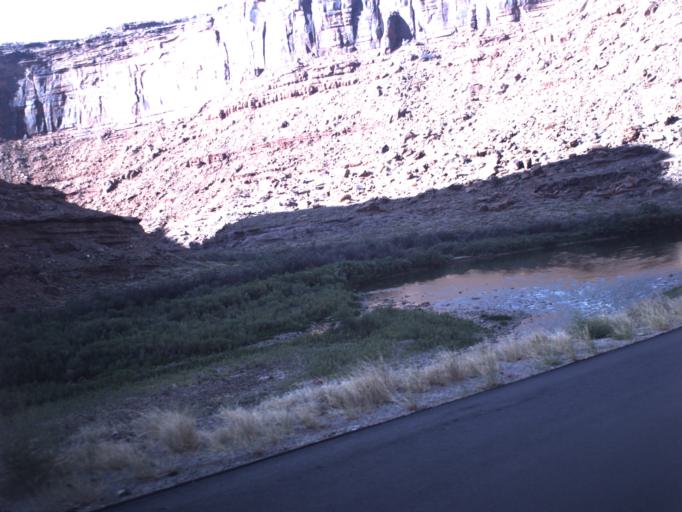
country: US
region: Utah
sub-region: Grand County
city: Moab
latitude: 38.6707
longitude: -109.4981
